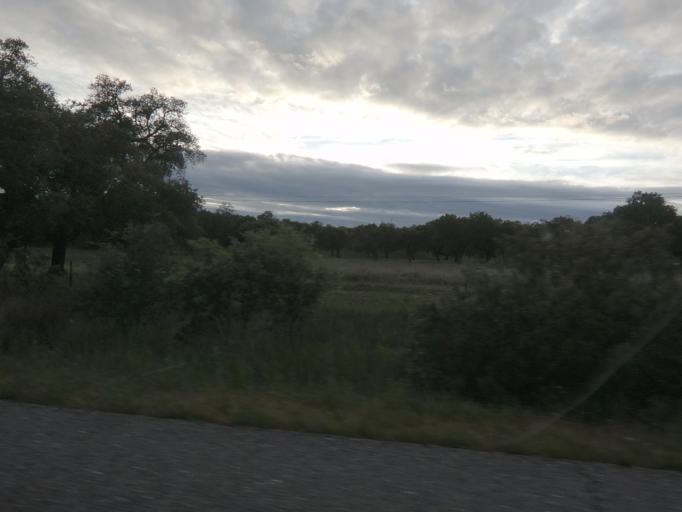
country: ES
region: Extremadura
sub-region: Provincia de Badajoz
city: Puebla de Obando
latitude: 39.1418
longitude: -6.6542
